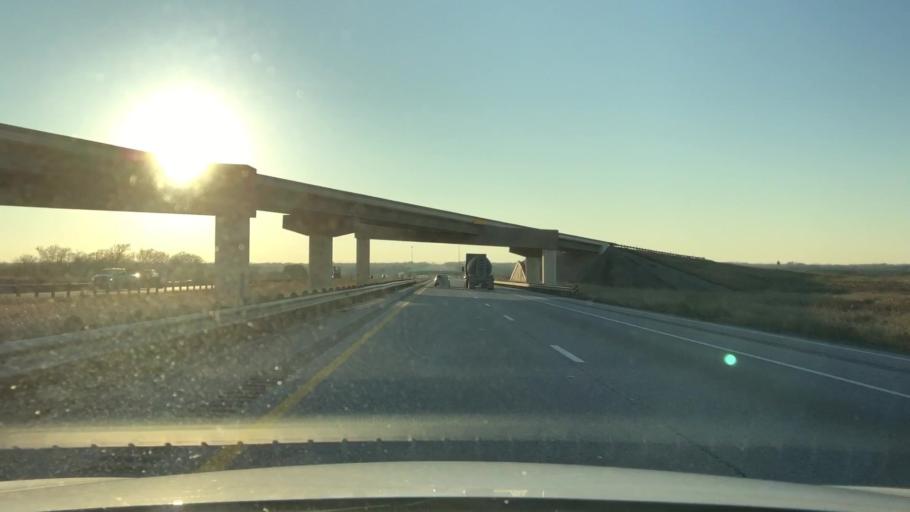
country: US
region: Texas
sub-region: Guadalupe County
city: Seguin
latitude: 29.6102
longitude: -97.8706
